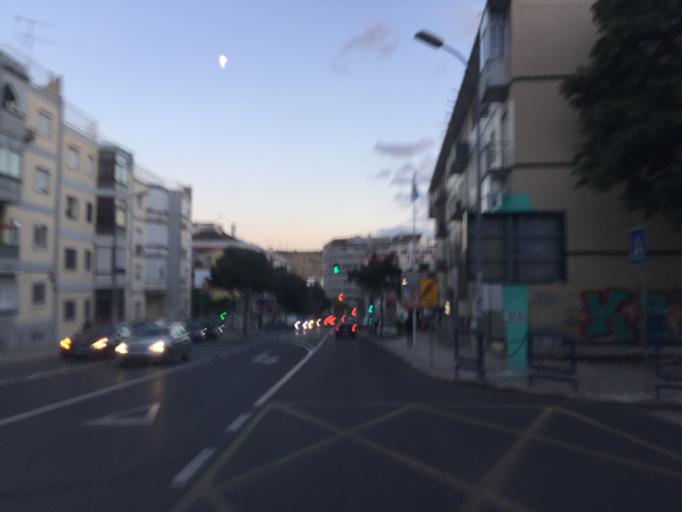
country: PT
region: Lisbon
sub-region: Odivelas
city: Odivelas
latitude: 38.7926
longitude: -9.1772
